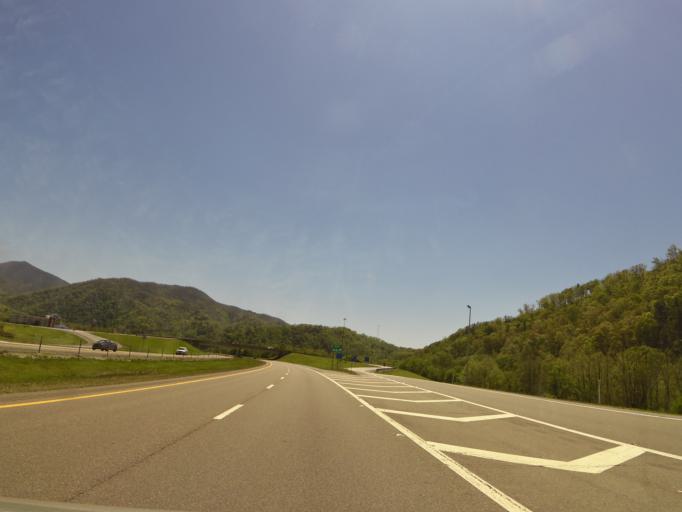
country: US
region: Tennessee
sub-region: Unicoi County
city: Banner Hill
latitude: 36.1255
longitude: -82.4451
